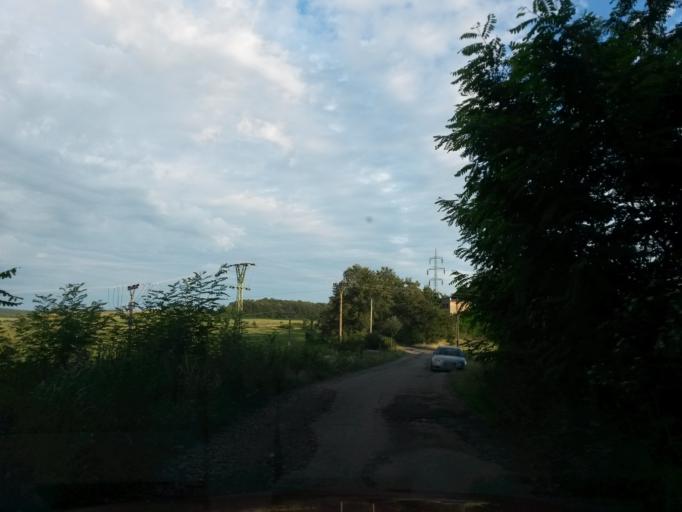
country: SK
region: Banskobystricky
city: Lucenec
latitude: 48.2898
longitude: 19.5020
